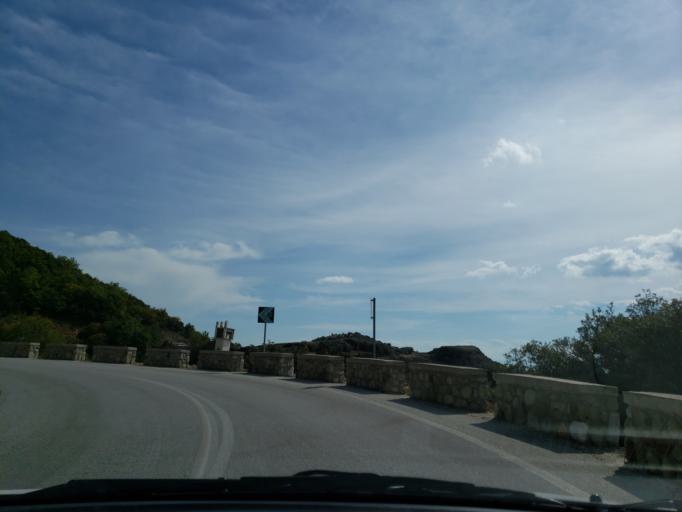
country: GR
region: Thessaly
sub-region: Trikala
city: Kastraki
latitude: 39.7204
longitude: 21.6362
